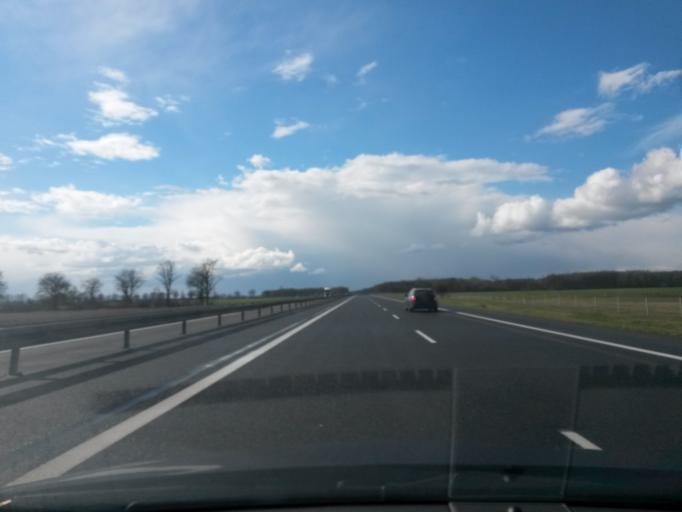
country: PL
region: Greater Poland Voivodeship
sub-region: Powiat wrzesinski
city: Wrzesnia
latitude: 52.3009
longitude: 17.6246
